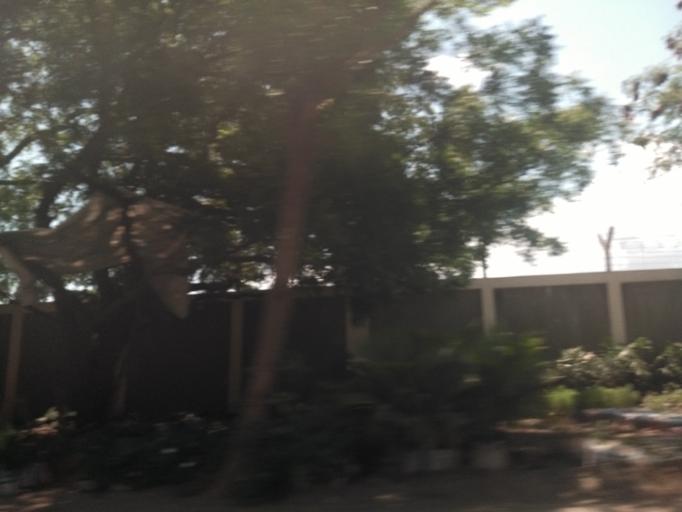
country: TZ
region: Dar es Salaam
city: Dar es Salaam
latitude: -6.8273
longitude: 39.2806
